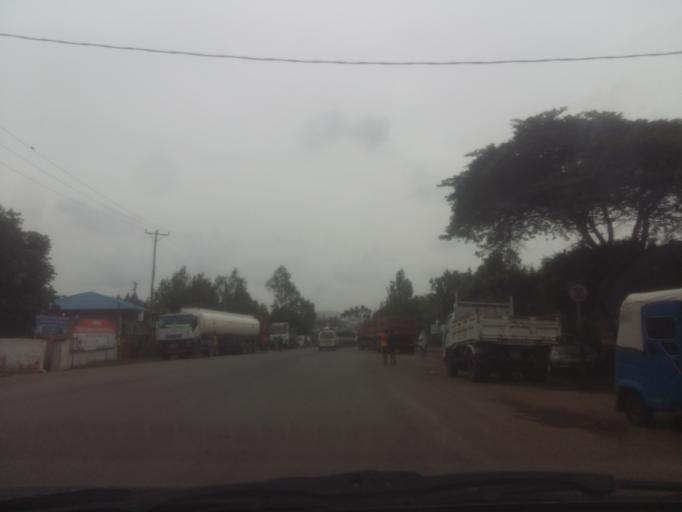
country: ET
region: Oromiya
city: Bishoftu
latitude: 8.7947
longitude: 38.8997
